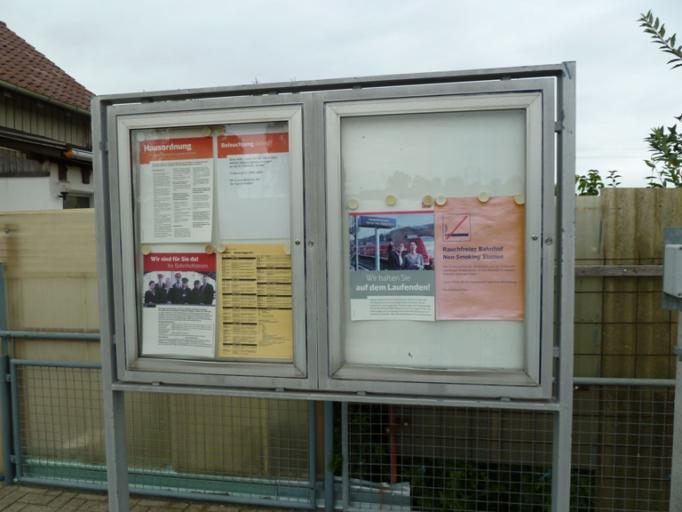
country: DE
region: Baden-Wuerttemberg
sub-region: Tuebingen Region
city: Herbertingen
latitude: 48.0539
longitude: 9.4331
